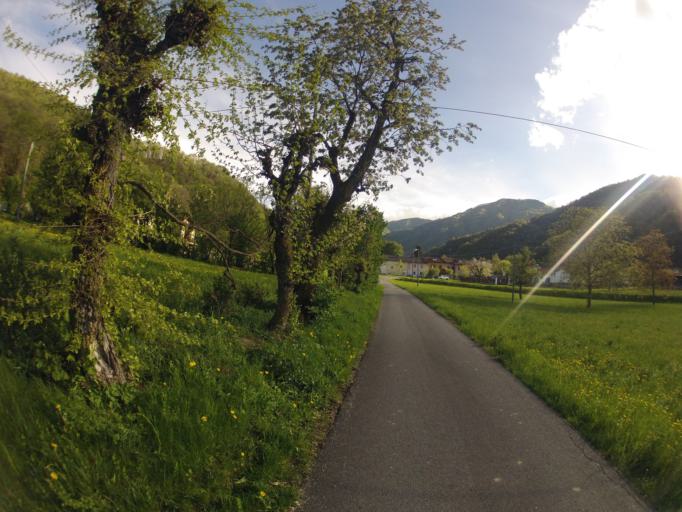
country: IT
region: Piedmont
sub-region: Provincia di Cuneo
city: Boves
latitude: 44.3052
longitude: 7.5732
